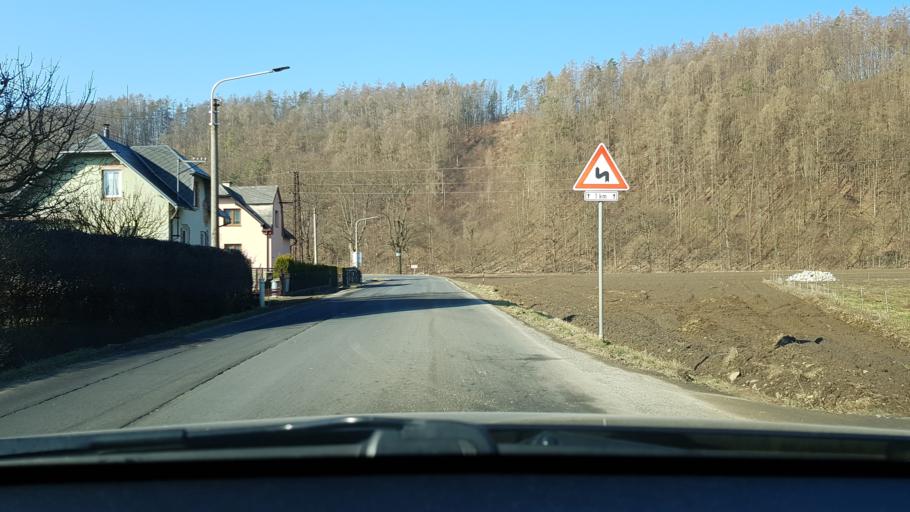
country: CZ
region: Olomoucky
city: Ruda nad Moravou
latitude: 49.9752
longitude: 16.8683
